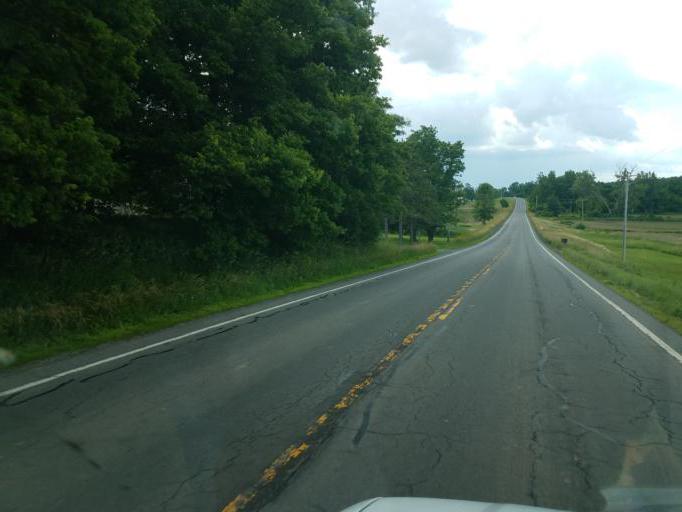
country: US
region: New York
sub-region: Wayne County
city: Clyde
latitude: 43.0329
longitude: -76.8623
